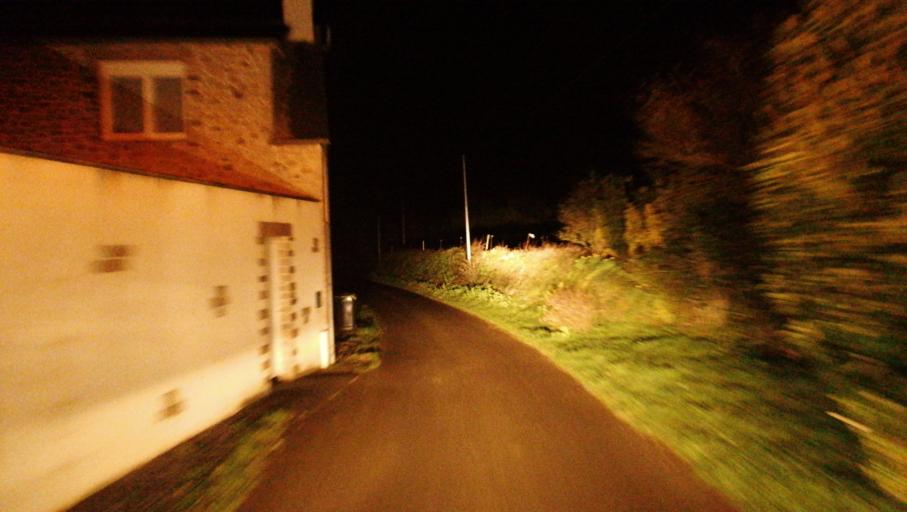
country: FR
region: Brittany
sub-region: Departement des Cotes-d'Armor
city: Lanvollon
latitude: 48.6386
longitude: -3.0072
